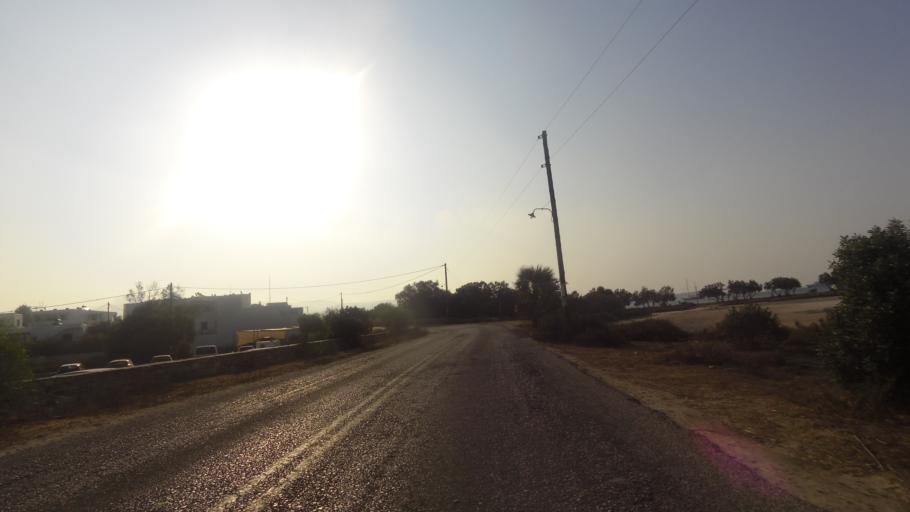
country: GR
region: South Aegean
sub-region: Nomos Kykladon
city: Antiparos
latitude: 37.0378
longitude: 25.0823
